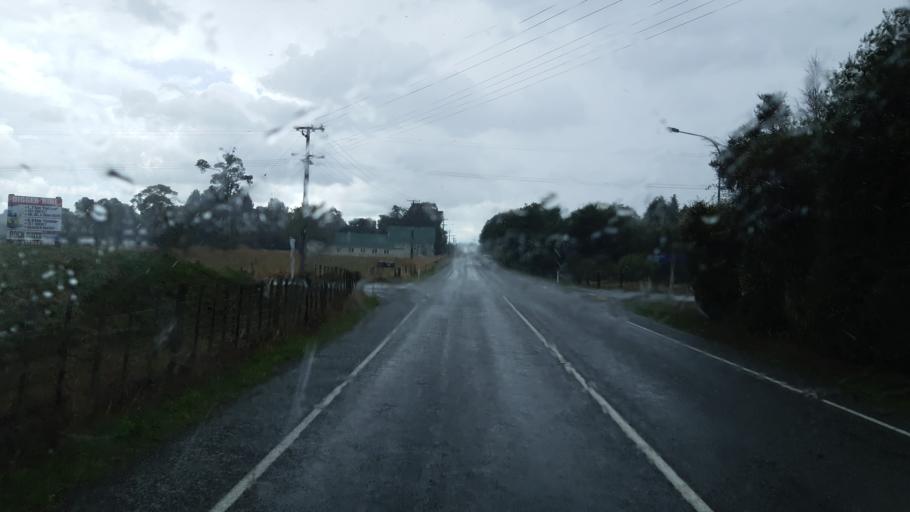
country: NZ
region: Tasman
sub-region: Tasman District
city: Wakefield
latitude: -41.3906
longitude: 173.0722
